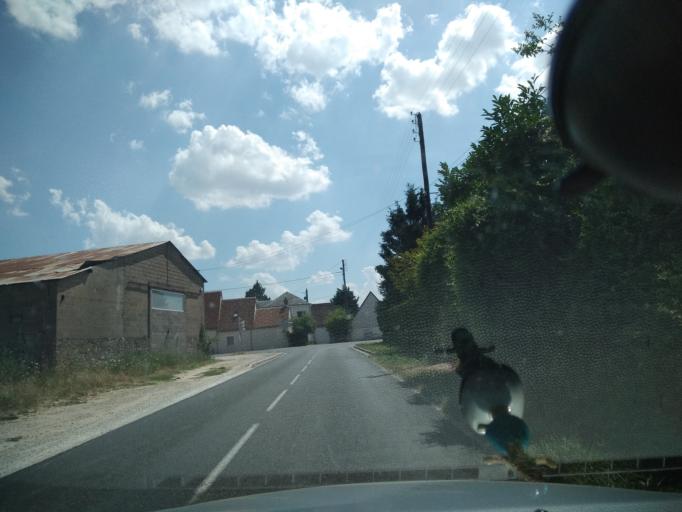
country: FR
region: Centre
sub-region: Departement d'Indre-et-Loire
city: Civray-de-Touraine
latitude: 47.3235
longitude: 1.0391
